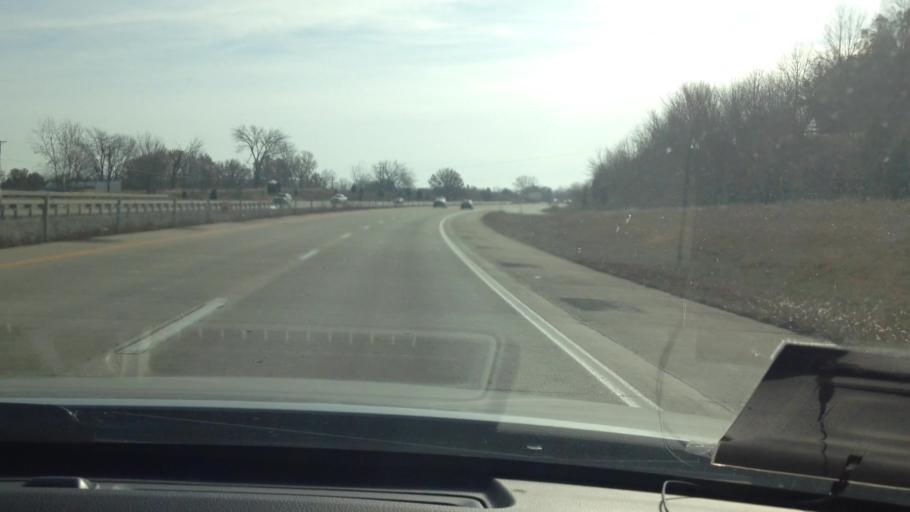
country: US
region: Missouri
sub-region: Cass County
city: Harrisonville
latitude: 38.6352
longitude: -94.3528
